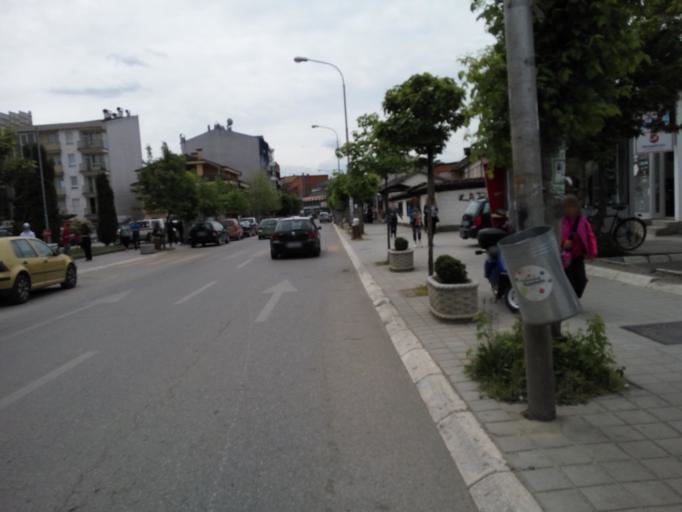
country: XK
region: Gjakova
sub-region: Komuna e Gjakoves
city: Gjakove
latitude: 42.3798
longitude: 20.4310
